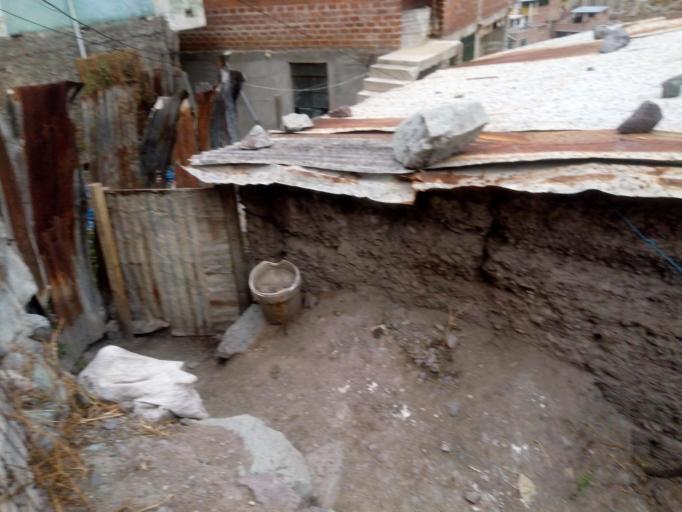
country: PE
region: Lima
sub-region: Provincia de Huarochiri
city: San Mateo
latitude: -11.7606
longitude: -76.3023
